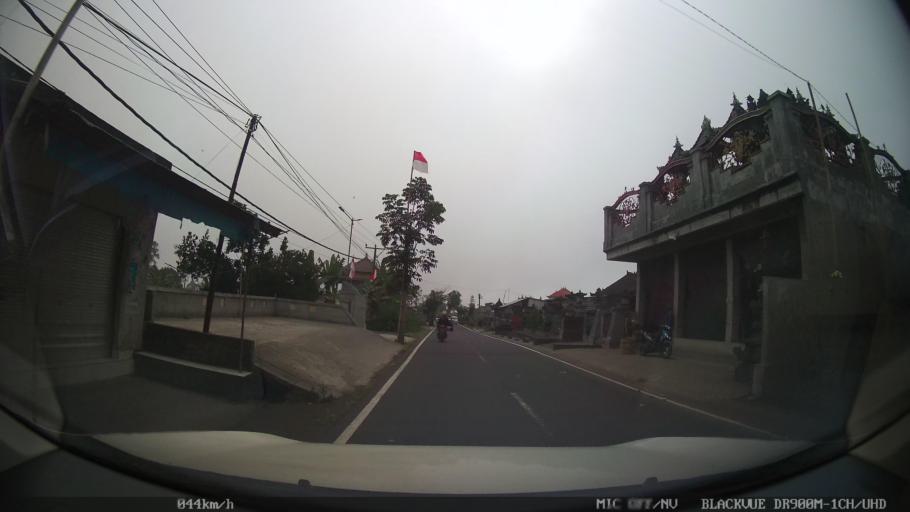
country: ID
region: Bali
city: Banjar Kedisan
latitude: -8.3008
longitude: 115.3093
